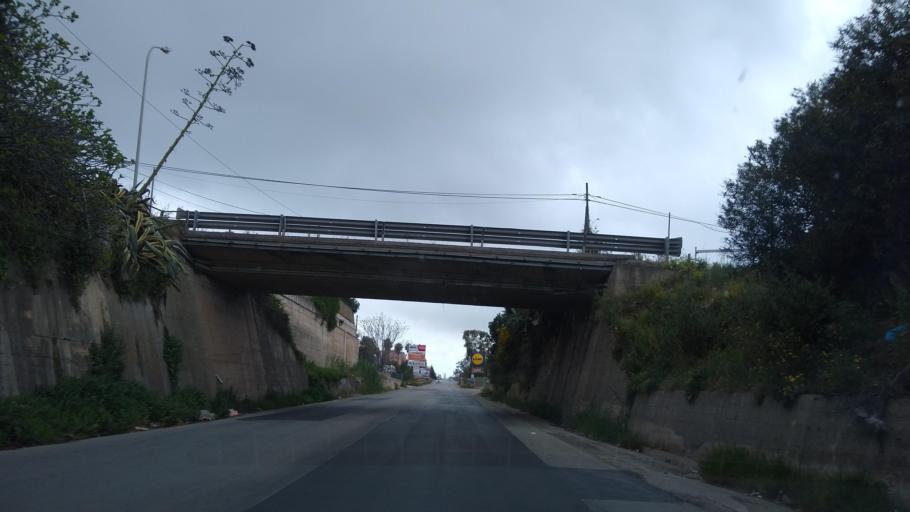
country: IT
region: Sicily
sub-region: Trapani
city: Alcamo
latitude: 37.9848
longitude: 12.9515
